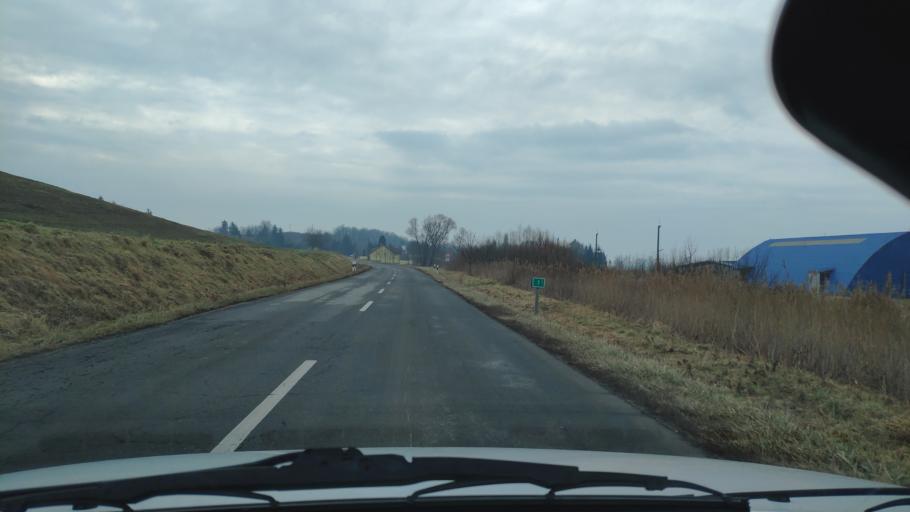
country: HU
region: Zala
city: Nagykanizsa
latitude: 46.5226
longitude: 16.9818
